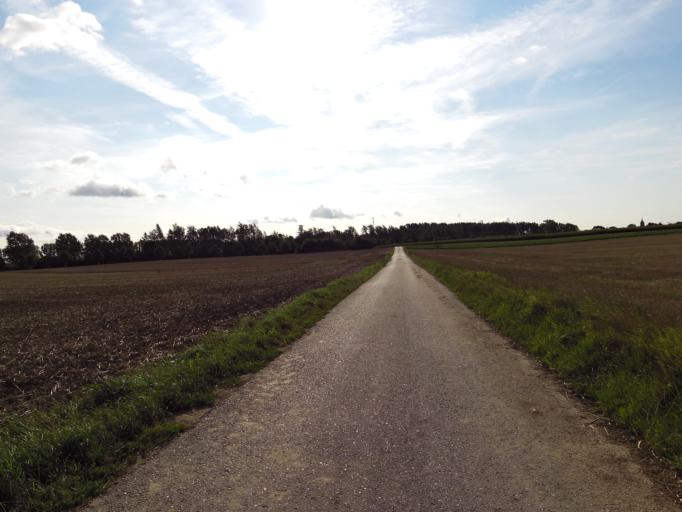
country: DE
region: North Rhine-Westphalia
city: Siersdorf
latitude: 50.9067
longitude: 6.2148
